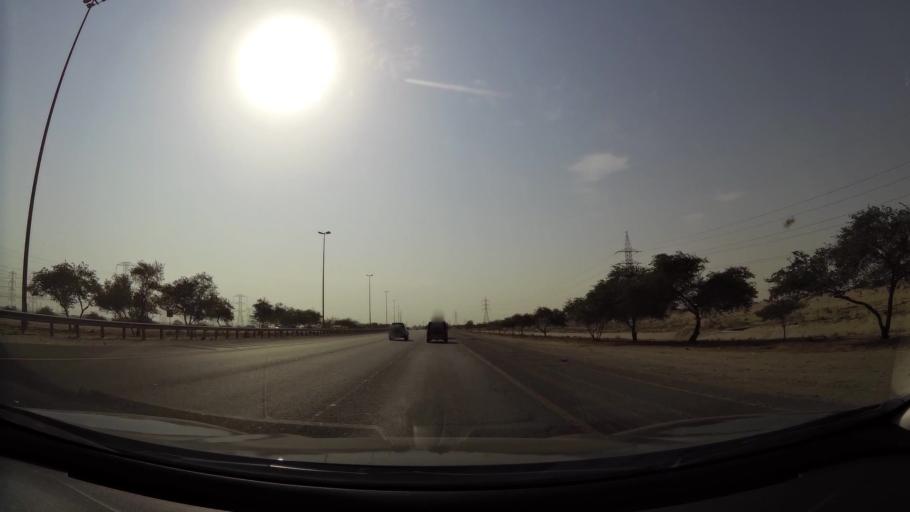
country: KW
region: Al Ahmadi
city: Al Ahmadi
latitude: 28.9712
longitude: 48.1134
